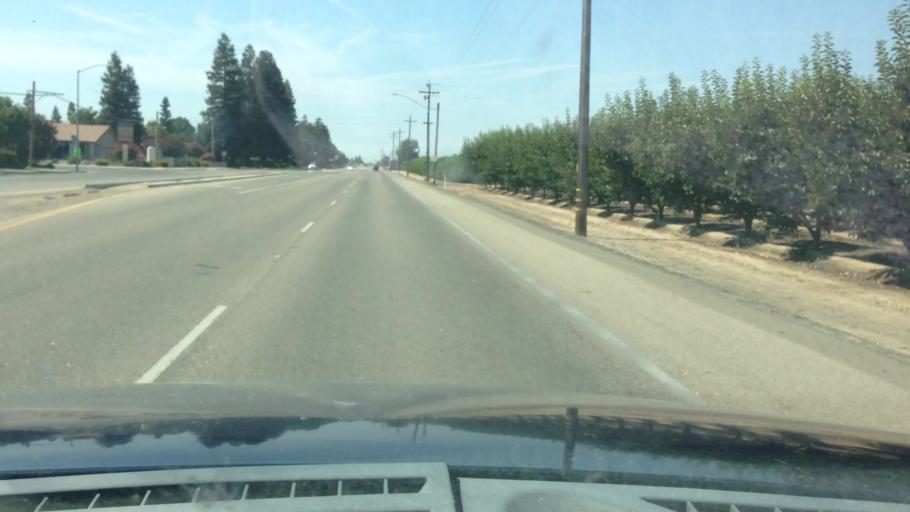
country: US
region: California
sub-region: Fresno County
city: Parlier
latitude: 36.6134
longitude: -119.5569
